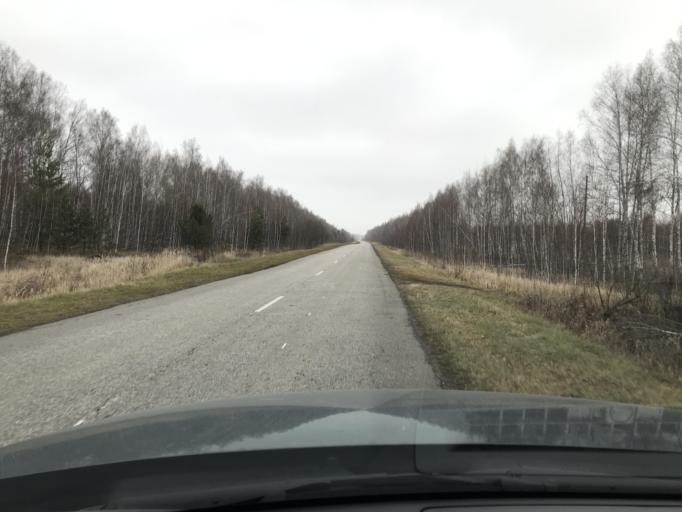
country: RU
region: Penza
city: Zemetchino
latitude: 53.6858
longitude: 42.6358
